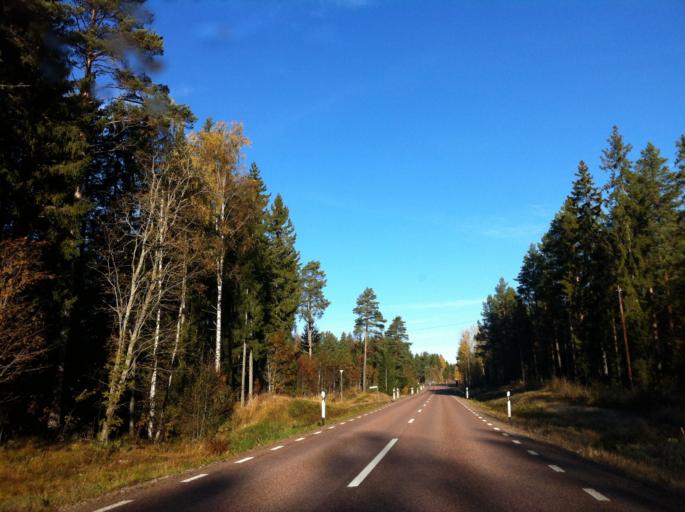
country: SE
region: Gaevleborg
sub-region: Gavle Kommun
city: Gavle
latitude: 60.5469
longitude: 17.1287
